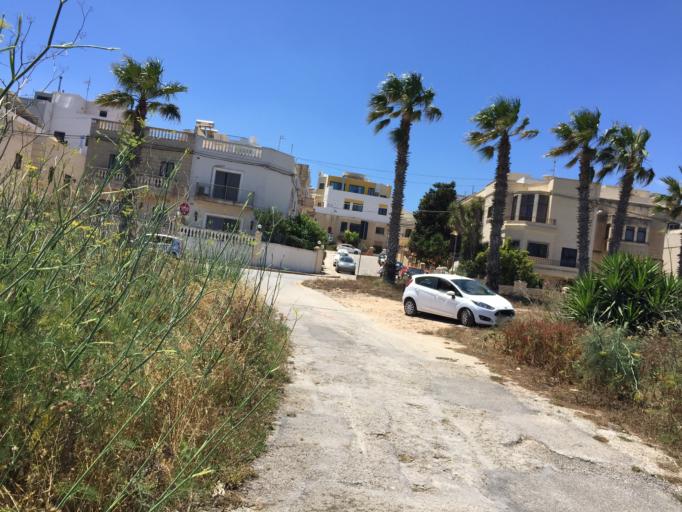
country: MT
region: Pembroke
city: Pembroke
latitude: 35.9290
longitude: 14.4835
